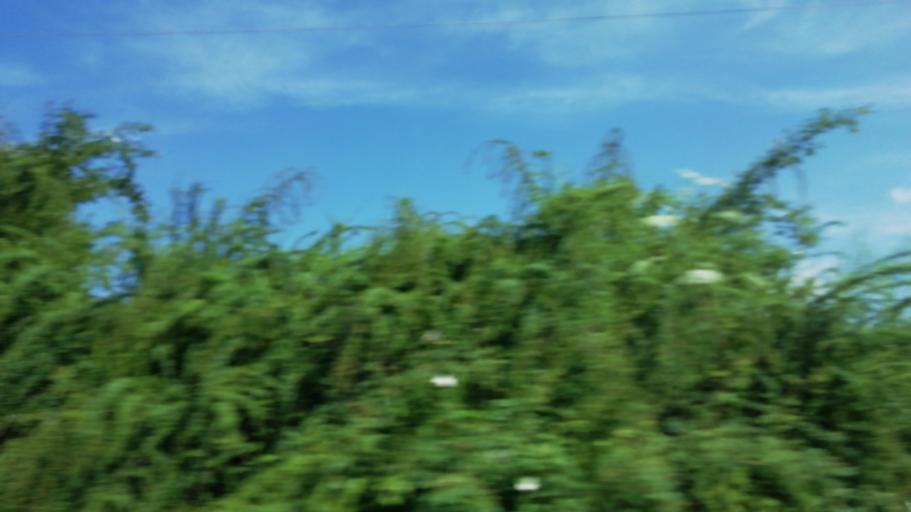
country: TR
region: Karabuk
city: Karabuk
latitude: 41.1053
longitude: 32.5969
